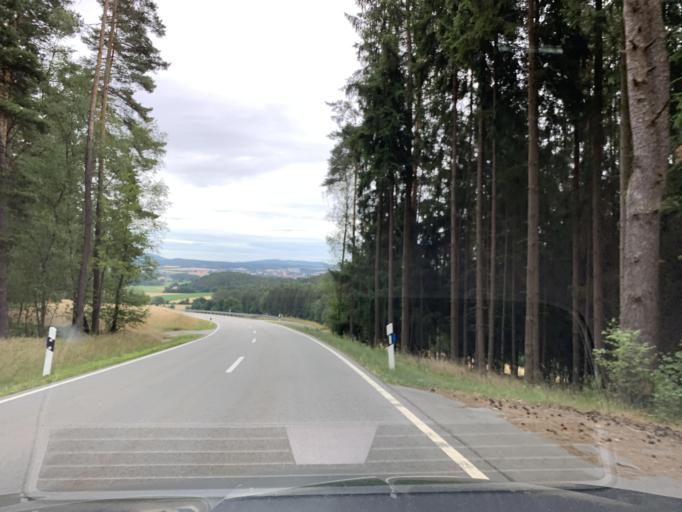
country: DE
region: Bavaria
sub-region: Upper Palatinate
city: Schwarzhofen
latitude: 49.3621
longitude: 12.3301
